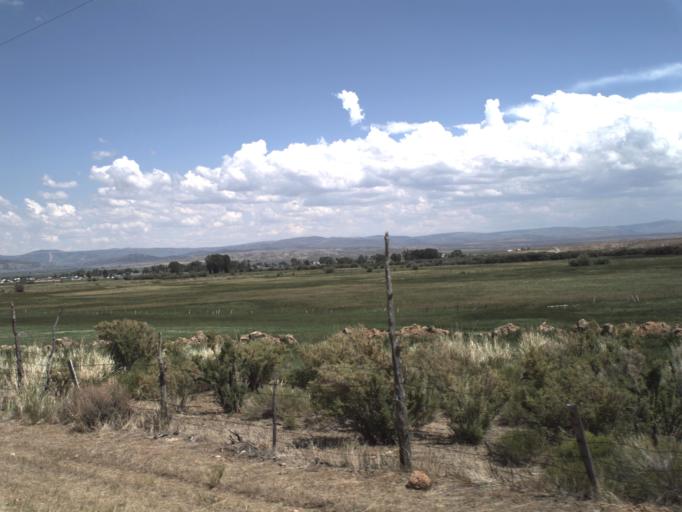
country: US
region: Utah
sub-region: Rich County
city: Randolph
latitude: 41.5206
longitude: -111.1925
